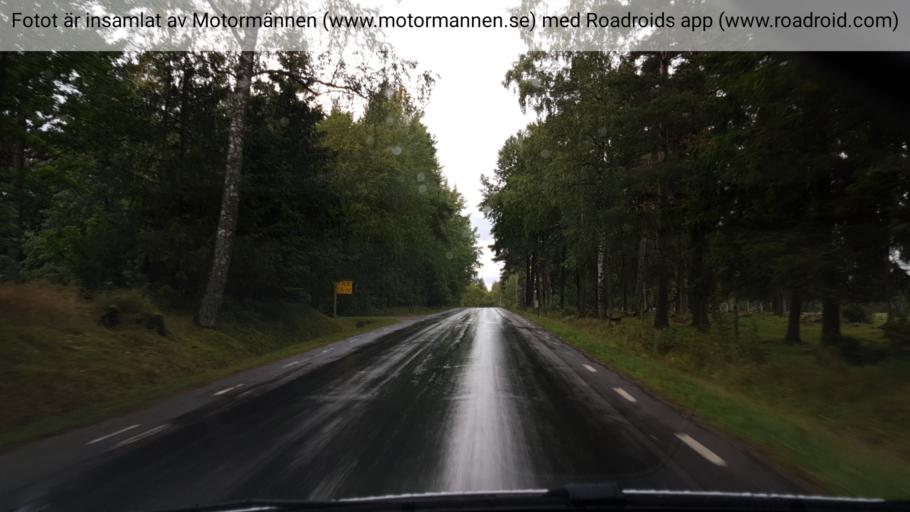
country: SE
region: Vaestra Goetaland
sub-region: Tidaholms Kommun
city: Olofstorp
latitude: 58.3046
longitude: 14.0337
